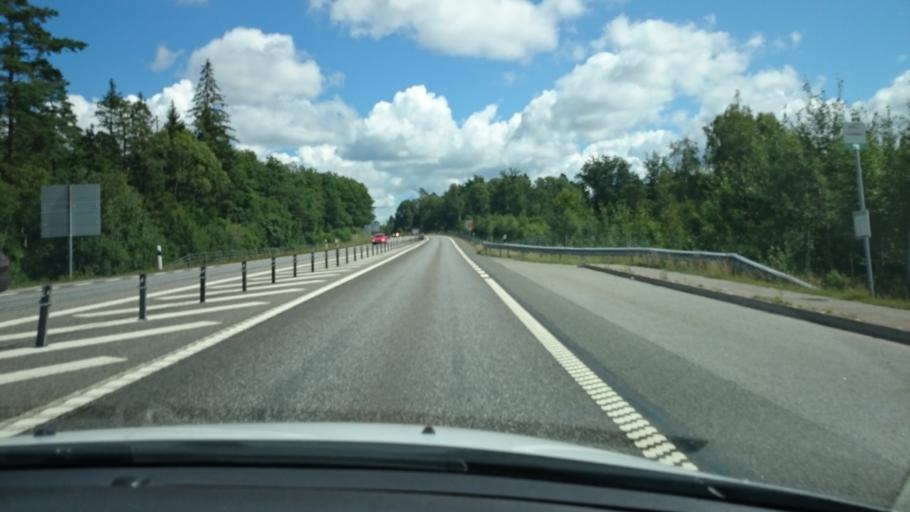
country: SE
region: Halland
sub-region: Hylte Kommun
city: Torup
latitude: 56.9712
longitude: 13.1634
